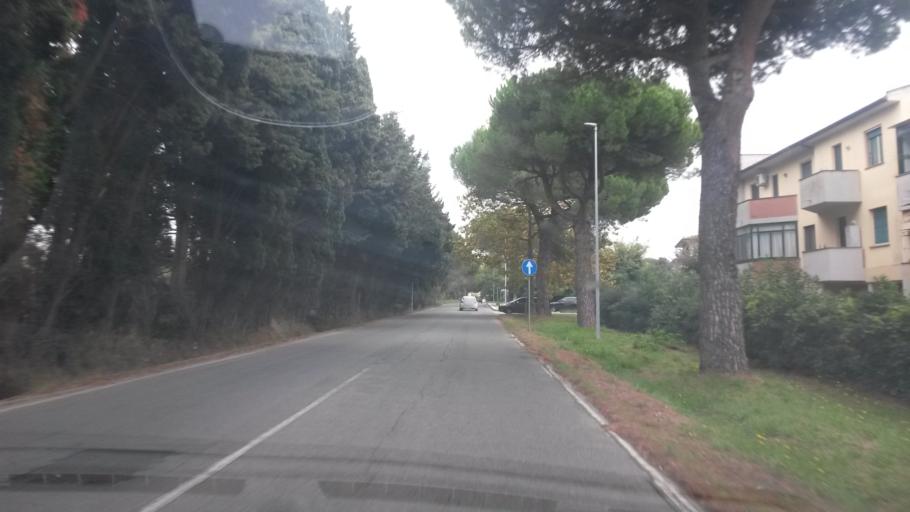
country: IT
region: Tuscany
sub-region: Provincia di Livorno
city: Rosignano Solvay-Castiglioncello
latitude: 43.4000
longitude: 10.4379
